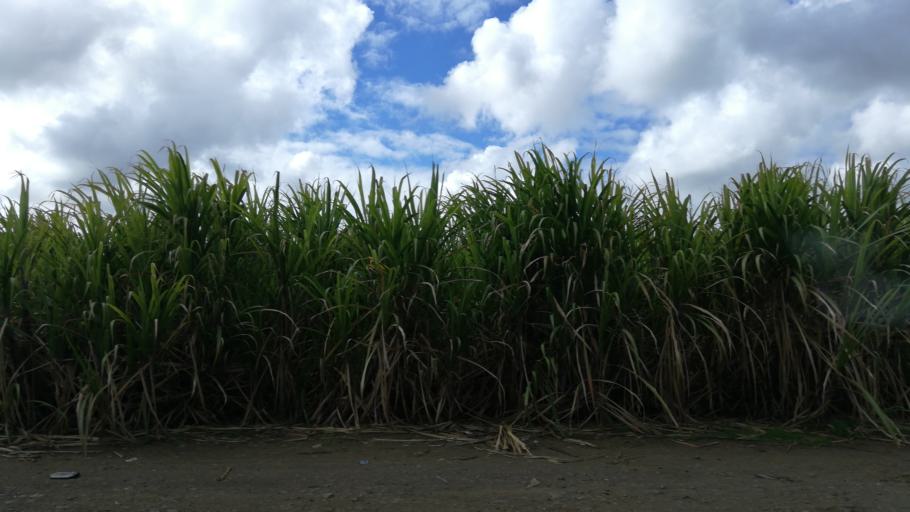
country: MU
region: Flacq
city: Lalmatie
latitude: -20.2115
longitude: 57.6769
